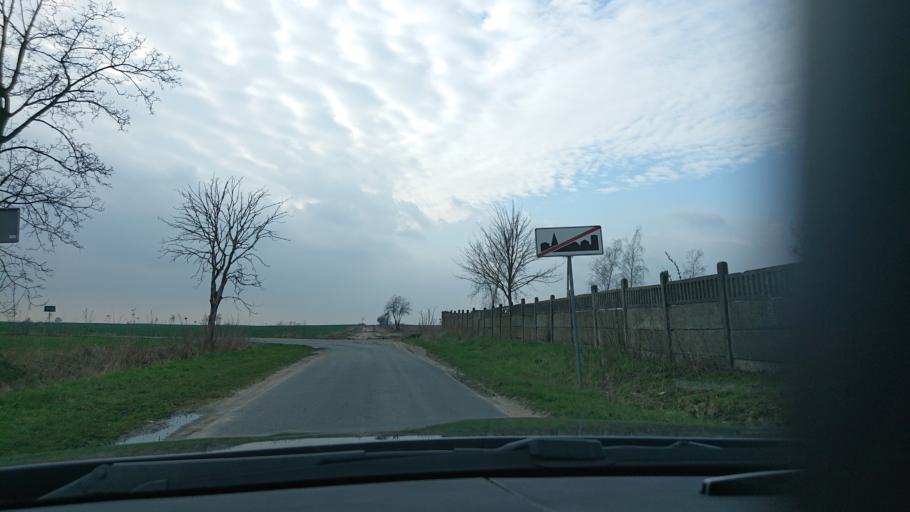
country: PL
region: Greater Poland Voivodeship
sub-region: Powiat gnieznienski
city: Gniezno
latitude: 52.5610
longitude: 17.5226
